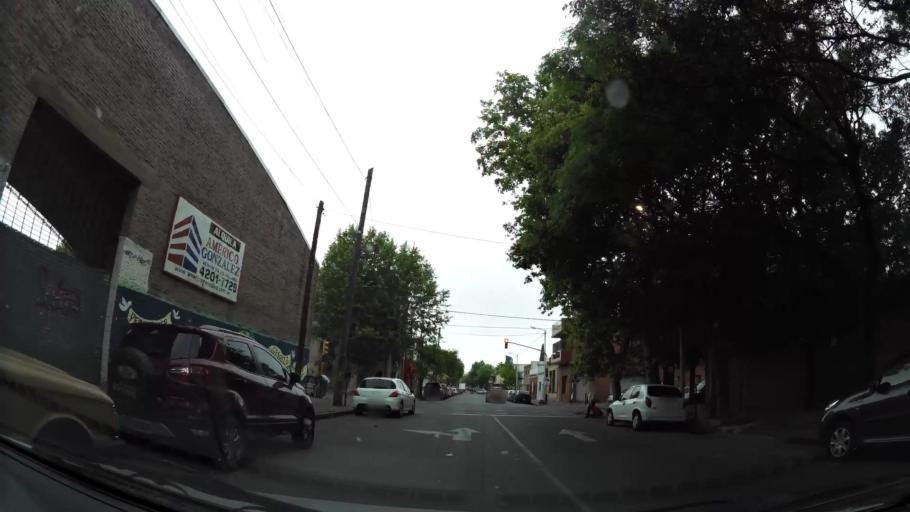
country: AR
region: Buenos Aires
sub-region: Partido de Avellaneda
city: Avellaneda
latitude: -34.6590
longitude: -58.3631
